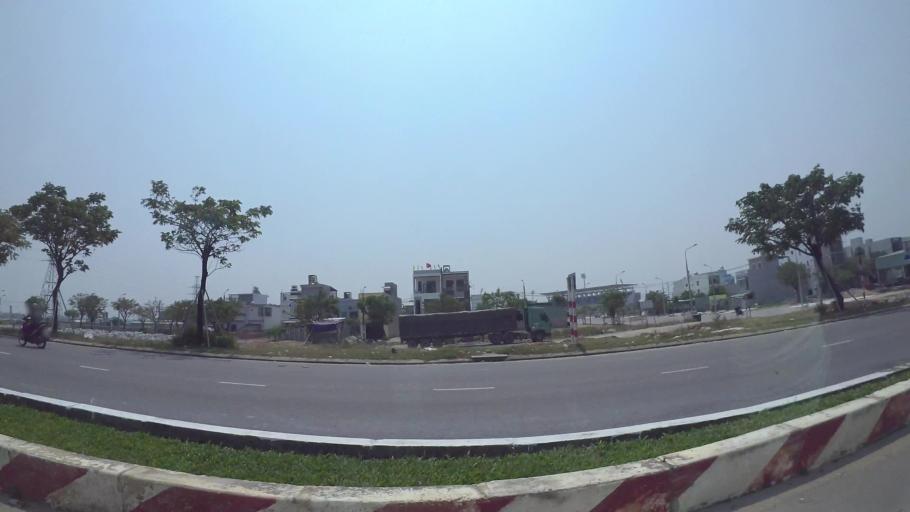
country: VN
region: Da Nang
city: Cam Le
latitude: 16.0029
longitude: 108.2264
